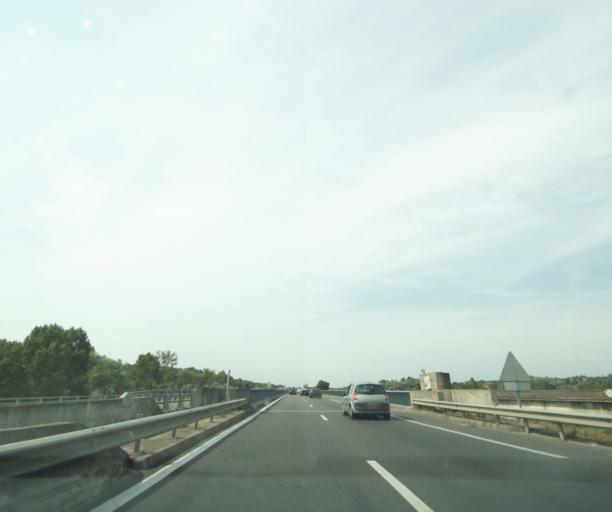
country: FR
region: Centre
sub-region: Departement d'Indre-et-Loire
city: Saint-Cyr-sur-Loire
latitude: 47.3896
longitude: 0.6486
